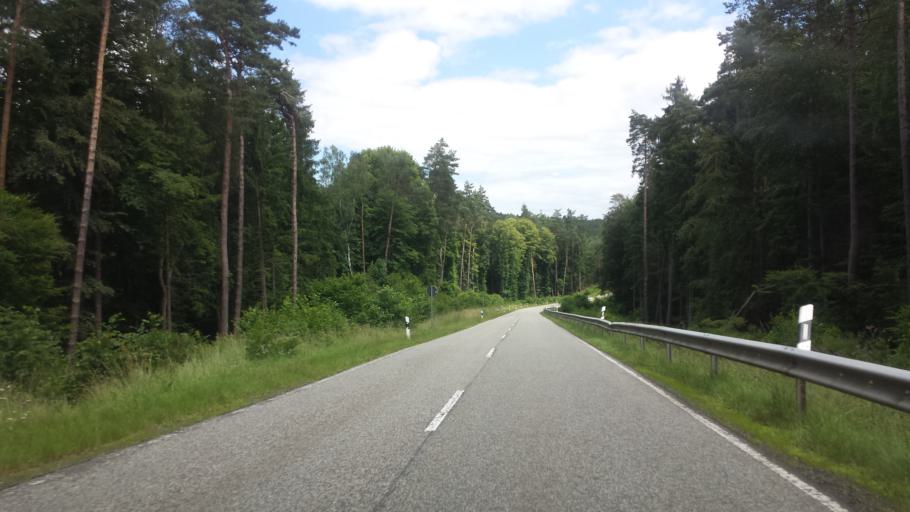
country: DE
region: Rheinland-Pfalz
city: Neuhemsbach
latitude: 49.5051
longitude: 7.9424
